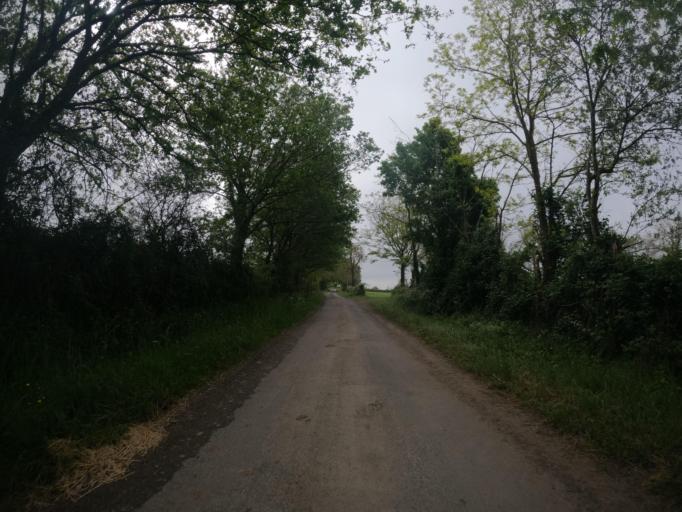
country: FR
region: Poitou-Charentes
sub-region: Departement des Deux-Sevres
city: Chiche
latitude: 46.8415
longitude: -0.3828
